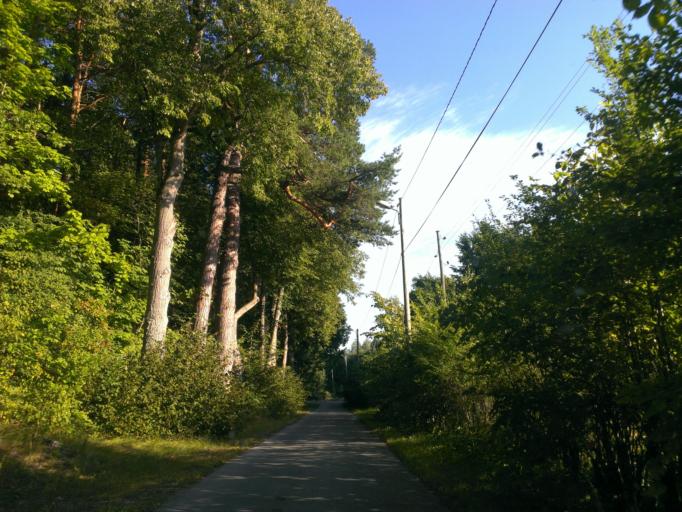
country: LV
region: Carnikava
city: Carnikava
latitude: 57.1241
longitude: 24.3216
